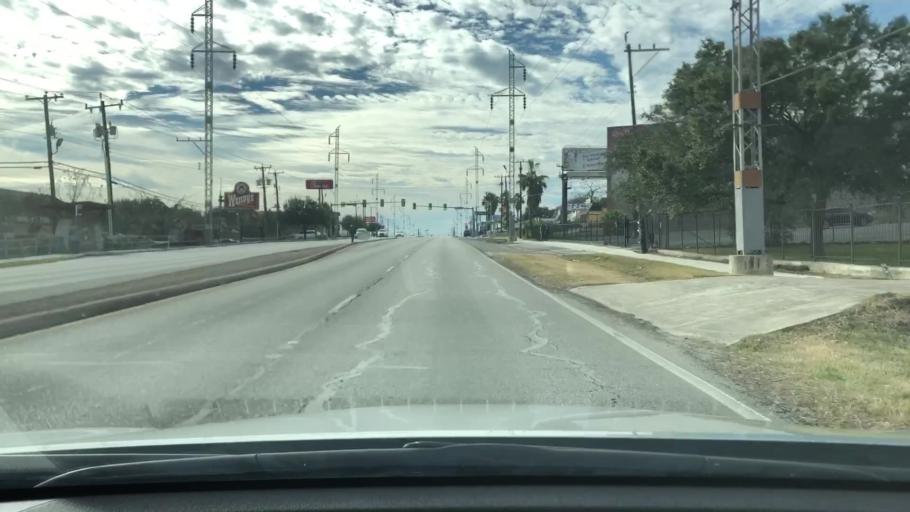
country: US
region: Texas
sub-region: Bexar County
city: Terrell Hills
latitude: 29.4919
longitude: -98.4379
